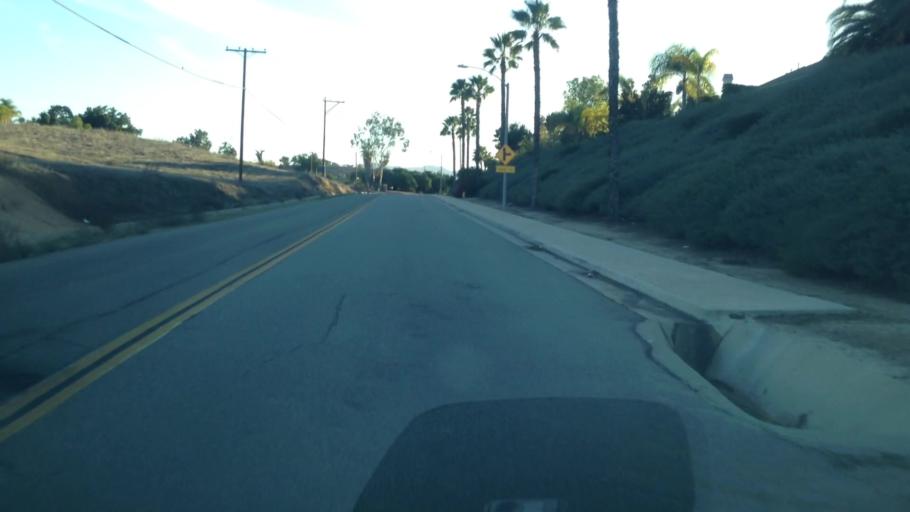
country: US
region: California
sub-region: Riverside County
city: Woodcrest
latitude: 33.8726
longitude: -117.4362
